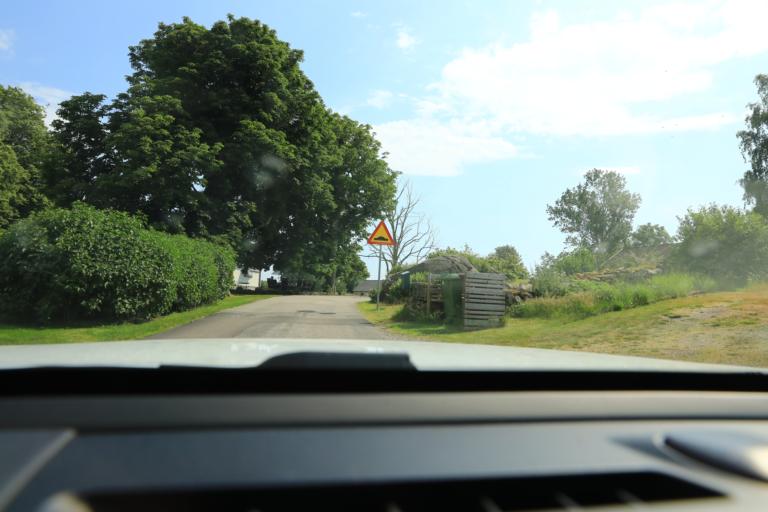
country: SE
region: Halland
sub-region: Varbergs Kommun
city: Varberg
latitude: 57.1590
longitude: 12.3152
